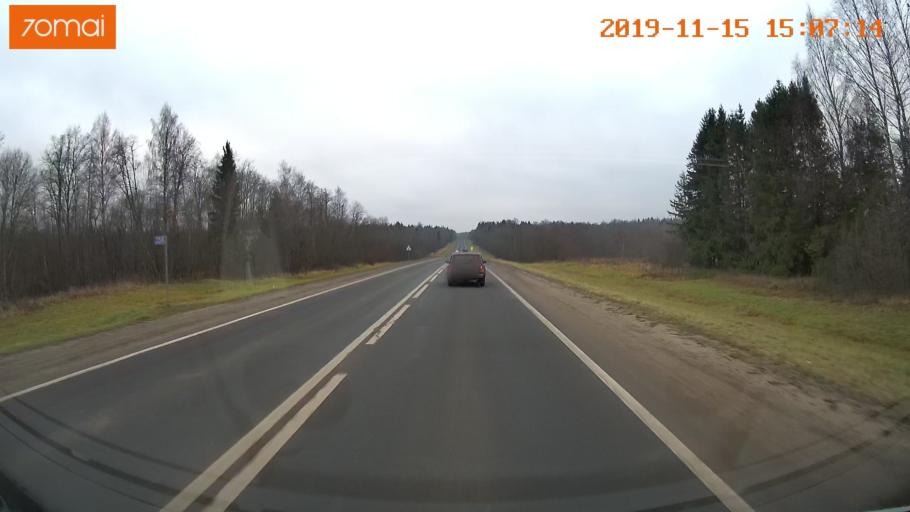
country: RU
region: Jaroslavl
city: Prechistoye
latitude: 58.3857
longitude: 40.2989
